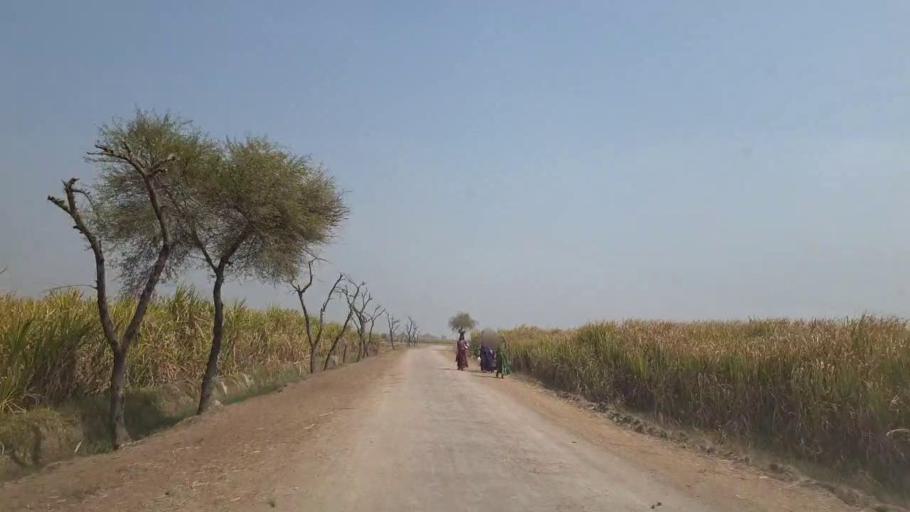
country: PK
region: Sindh
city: Mirpur Khas
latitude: 25.5459
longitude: 69.0869
